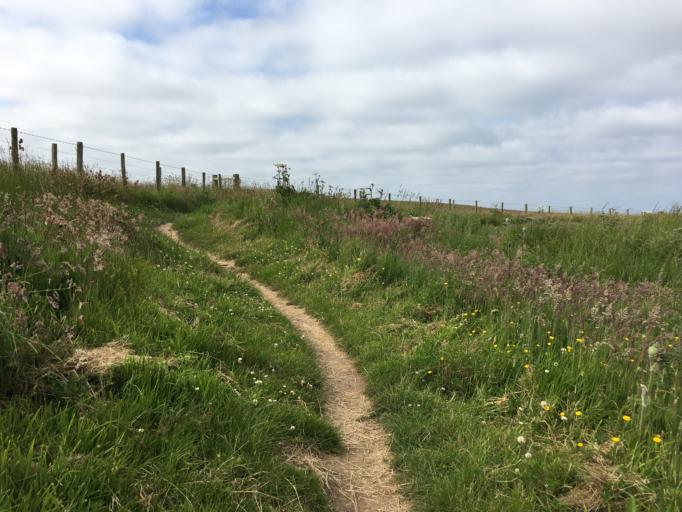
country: GB
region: England
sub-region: Northumberland
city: Alnmouth
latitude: 55.4447
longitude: -1.5903
